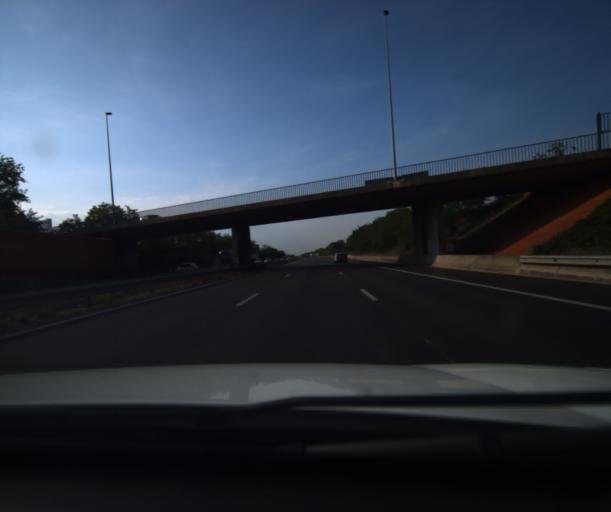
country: FR
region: Midi-Pyrenees
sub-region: Departement de la Haute-Garonne
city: Saint-Alban
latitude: 43.6879
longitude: 1.4121
